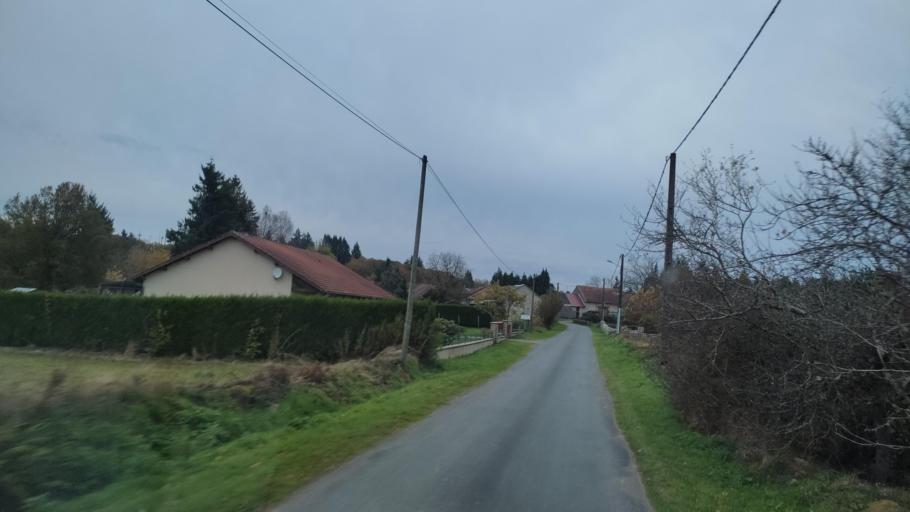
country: FR
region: Limousin
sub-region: Departement de la Haute-Vienne
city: Ambazac
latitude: 46.0316
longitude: 1.4670
